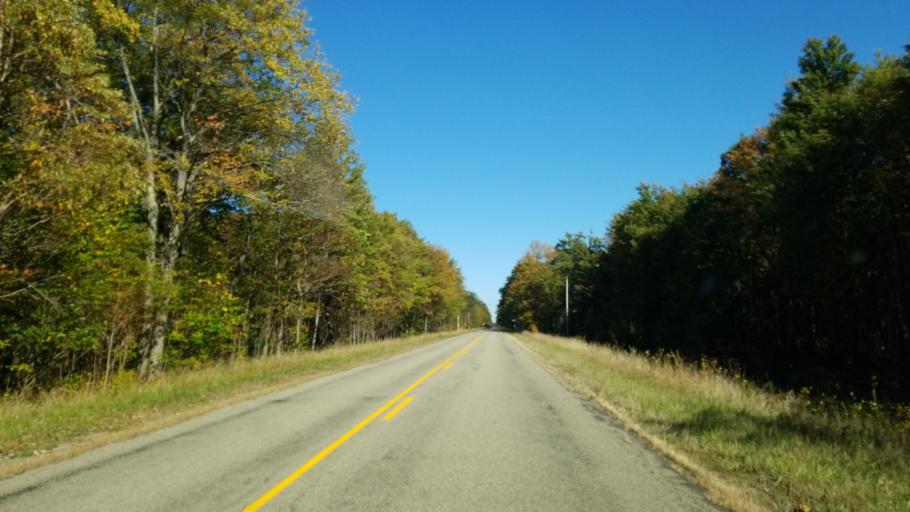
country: US
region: Pennsylvania
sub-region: Clearfield County
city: Shiloh
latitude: 41.2567
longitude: -78.3211
